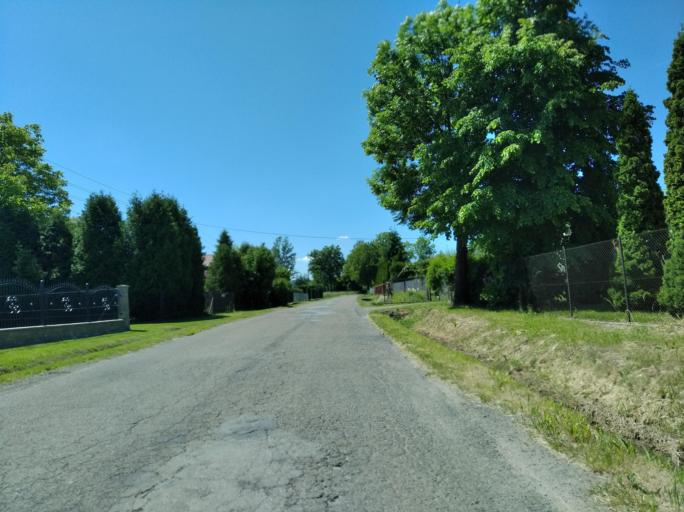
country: PL
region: Subcarpathian Voivodeship
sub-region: Powiat jasielski
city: Nowy Zmigrod
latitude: 49.6323
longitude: 21.5904
